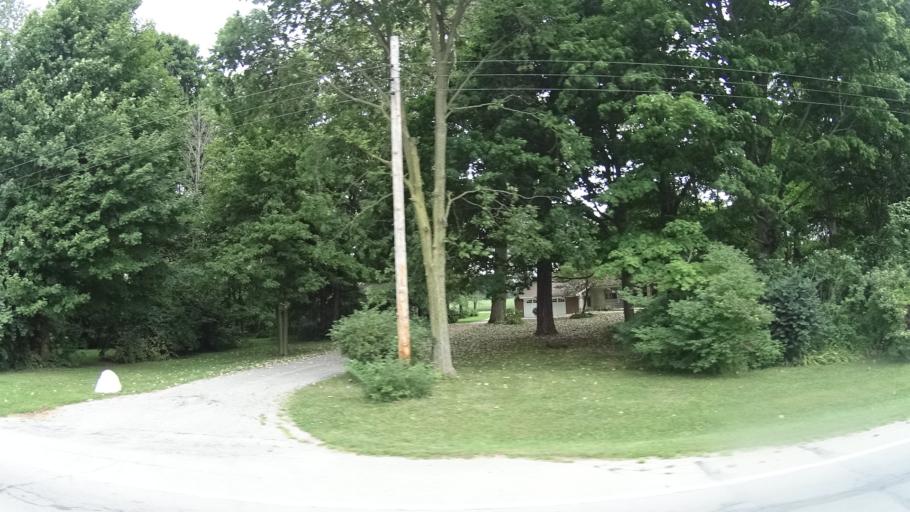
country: US
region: Indiana
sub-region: Madison County
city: Edgewood
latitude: 40.1013
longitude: -85.7543
